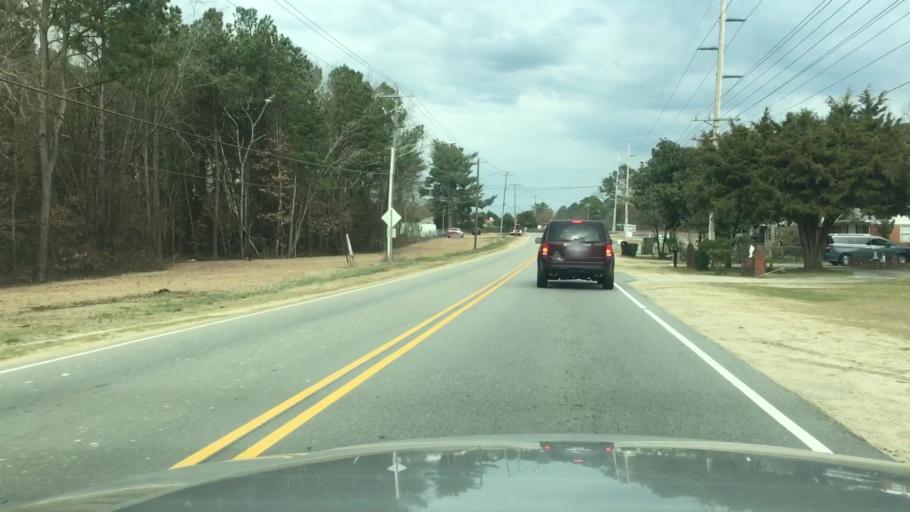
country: US
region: North Carolina
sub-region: Hoke County
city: Rockfish
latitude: 35.0220
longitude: -79.0024
